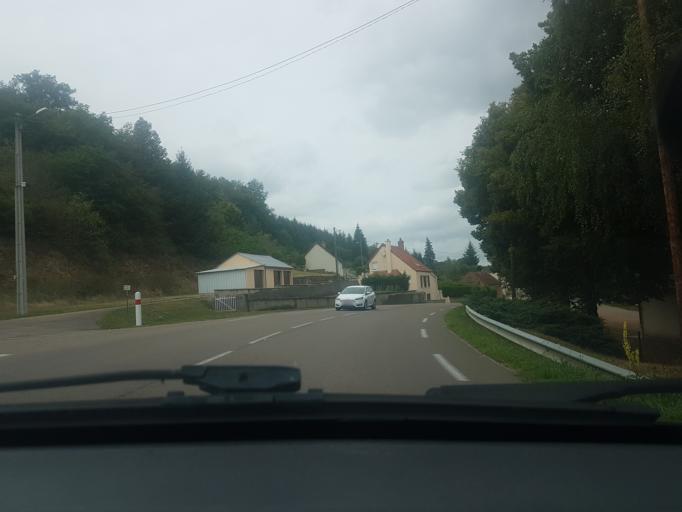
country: FR
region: Bourgogne
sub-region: Departement de la Cote-d'Or
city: Arnay-le-Duc
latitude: 47.1521
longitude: 4.4490
